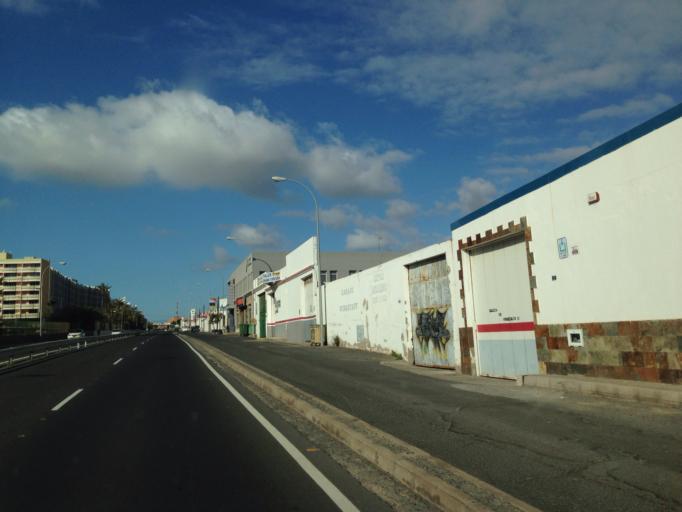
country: ES
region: Canary Islands
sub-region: Provincia de Las Palmas
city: Playa del Ingles
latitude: 27.7647
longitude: -15.5657
